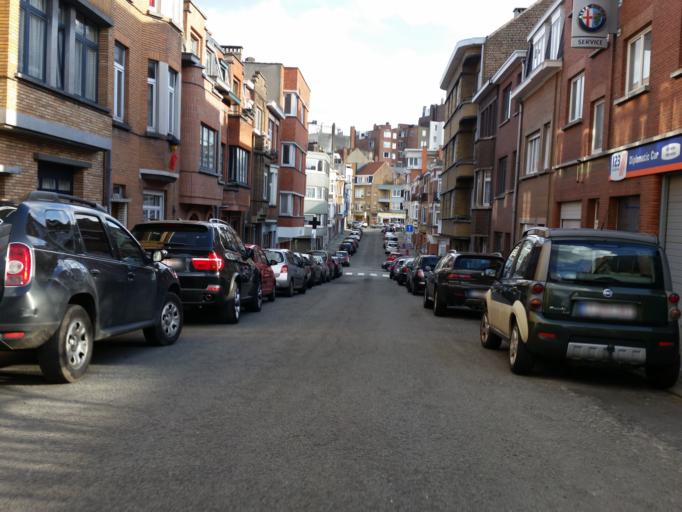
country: BE
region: Flanders
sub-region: Provincie Vlaams-Brabant
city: Diegem
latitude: 50.8433
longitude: 4.4135
